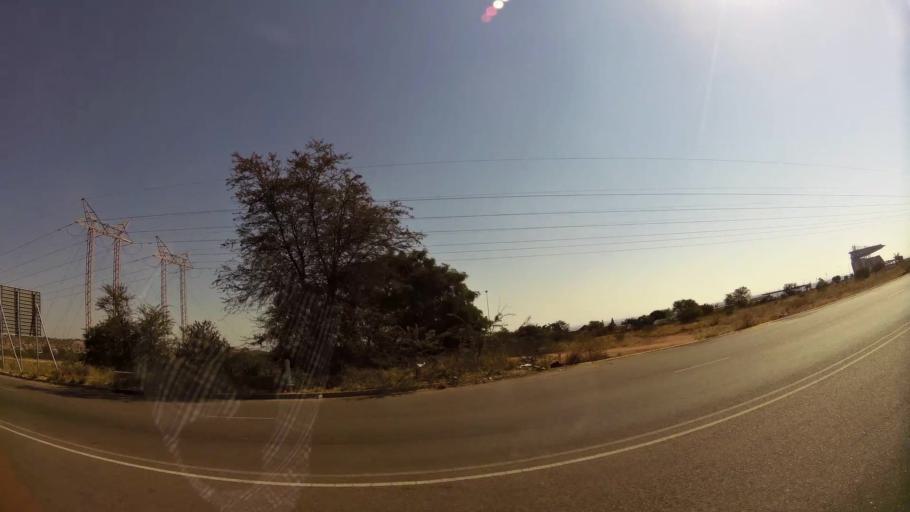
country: ZA
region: Gauteng
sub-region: City of Tshwane Metropolitan Municipality
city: Mabopane
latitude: -25.5232
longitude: 28.0880
